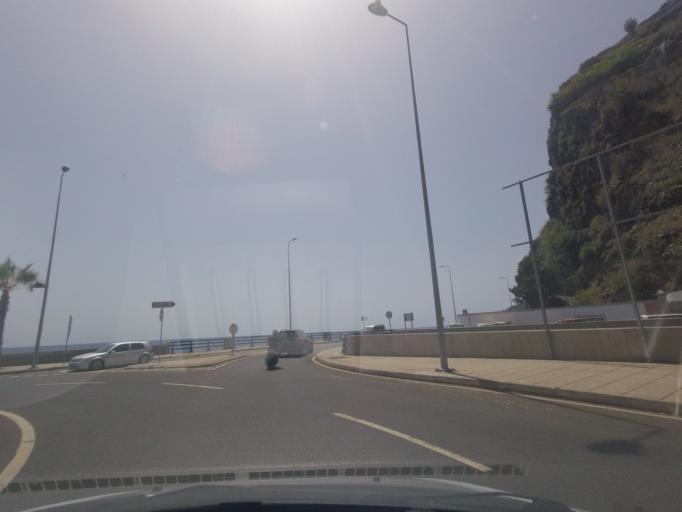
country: PT
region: Madeira
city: Ponta do Sol
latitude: 32.6774
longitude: -17.0785
